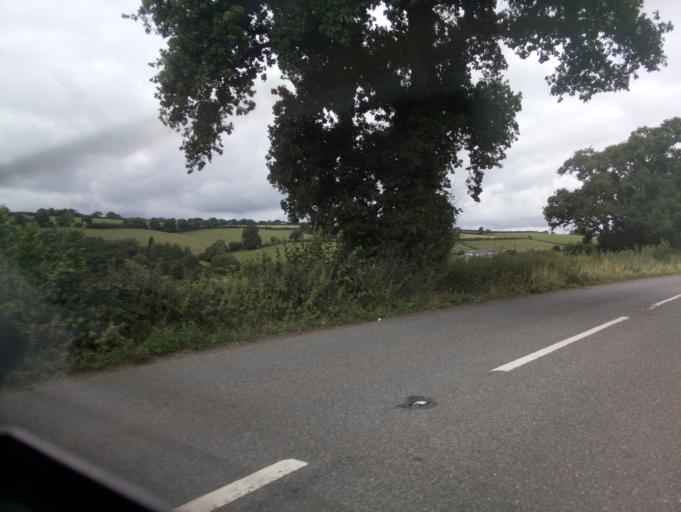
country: GB
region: England
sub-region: Devon
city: Cullompton
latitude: 50.8347
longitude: -3.3925
